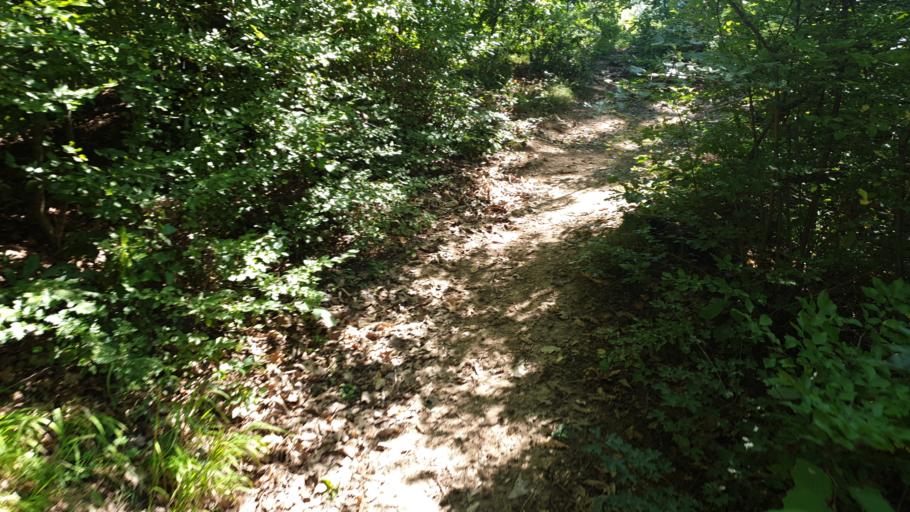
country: BA
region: Federation of Bosnia and Herzegovina
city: Polje-Bijela
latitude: 43.5264
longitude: 18.0803
